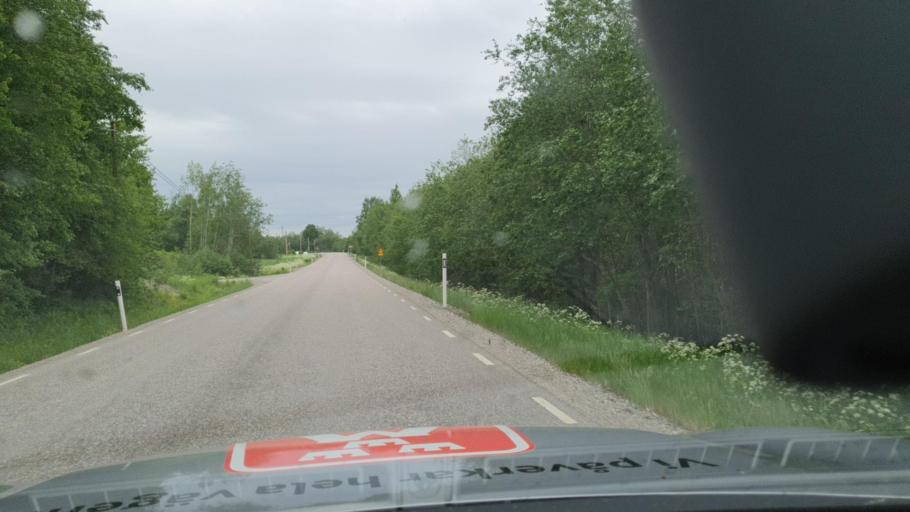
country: SE
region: Vaesternorrland
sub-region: Kramfors Kommun
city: Kramfors
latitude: 62.9372
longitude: 17.9052
